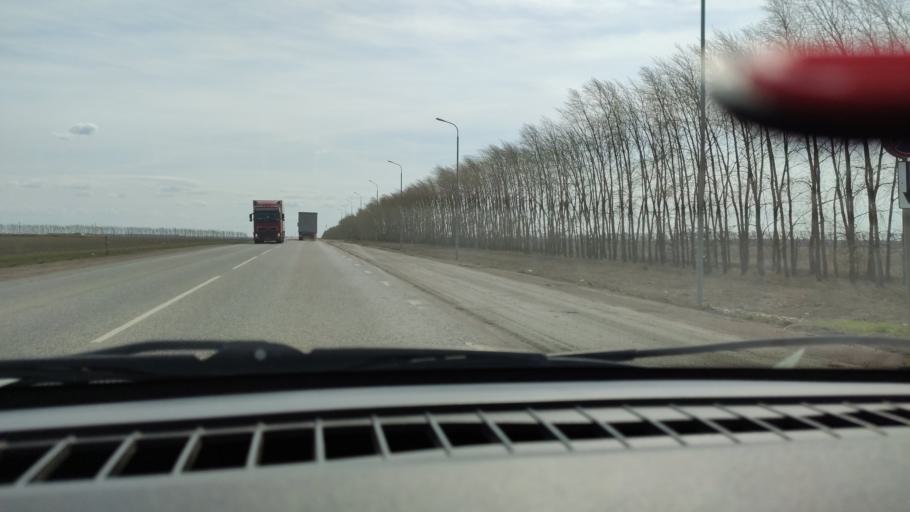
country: RU
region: Bashkortostan
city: Dyurtyuli
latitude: 55.3740
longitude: 54.8758
